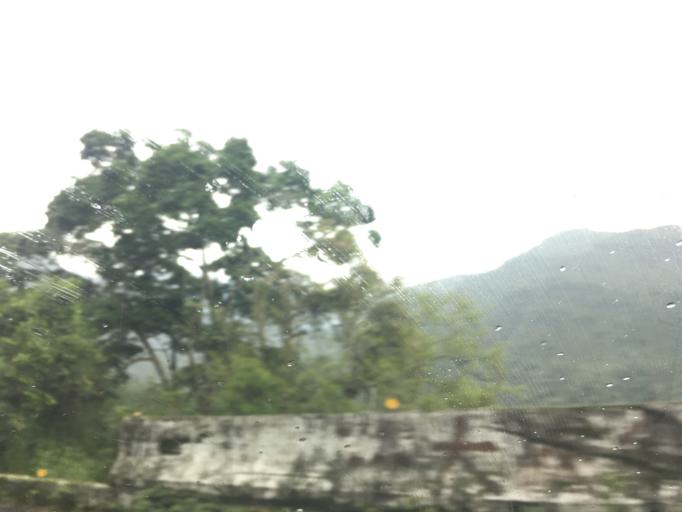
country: TW
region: Taiwan
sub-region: Yunlin
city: Douliu
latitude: 23.5680
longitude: 120.6379
